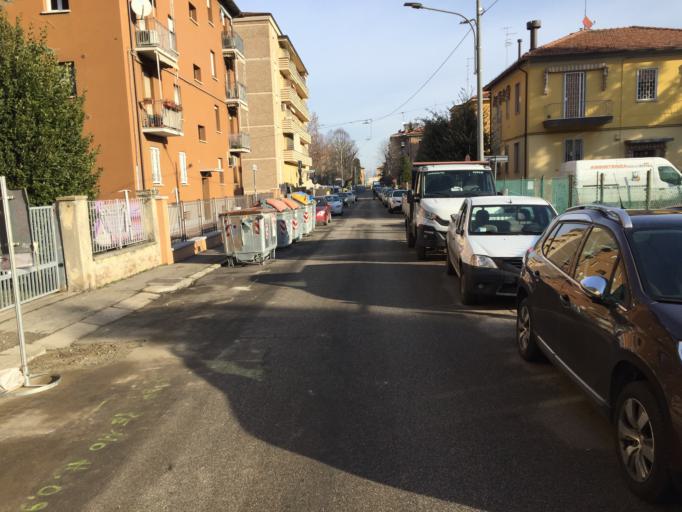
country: IT
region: Emilia-Romagna
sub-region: Provincia di Bologna
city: Casalecchio di Reno
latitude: 44.5190
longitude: 11.2740
